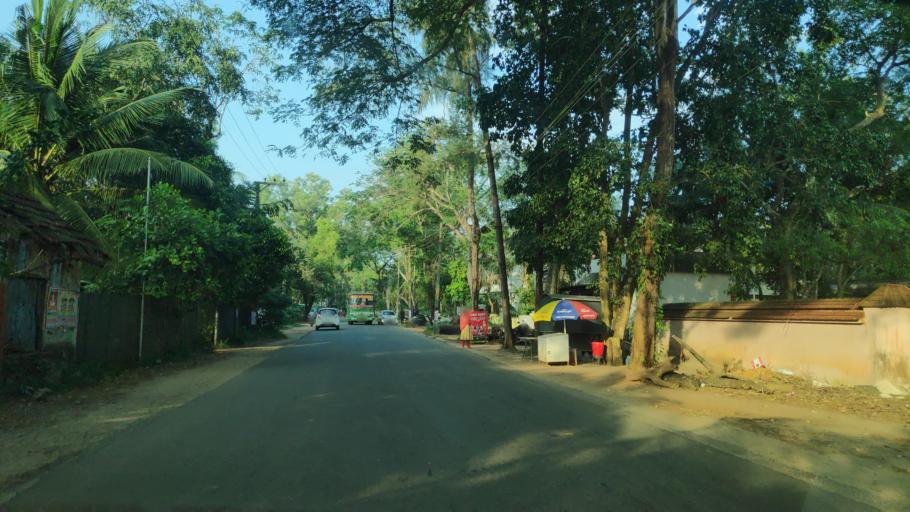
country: IN
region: Kerala
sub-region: Alappuzha
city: Shertallai
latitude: 9.6088
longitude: 76.3612
